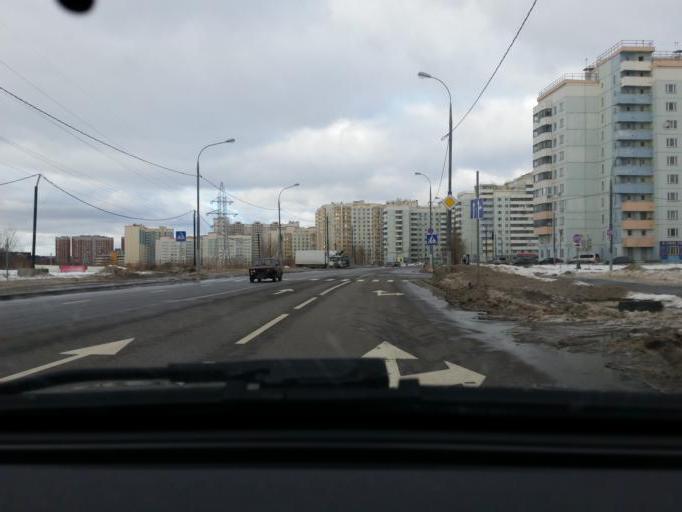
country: RU
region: Moskovskaya
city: Shcherbinka
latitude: 55.5003
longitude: 37.5886
